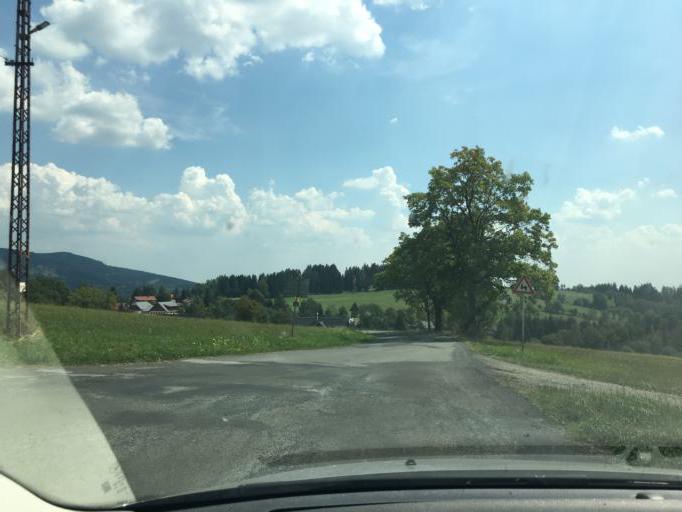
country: CZ
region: Liberecky
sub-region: Okres Semily
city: Ponikla
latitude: 50.6797
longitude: 15.5021
